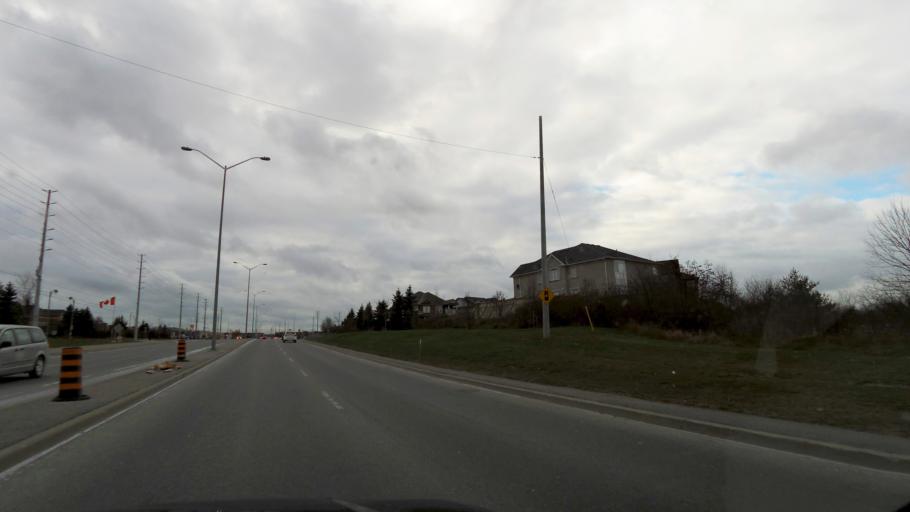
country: CA
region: Ontario
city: Brampton
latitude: 43.7656
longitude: -79.7197
